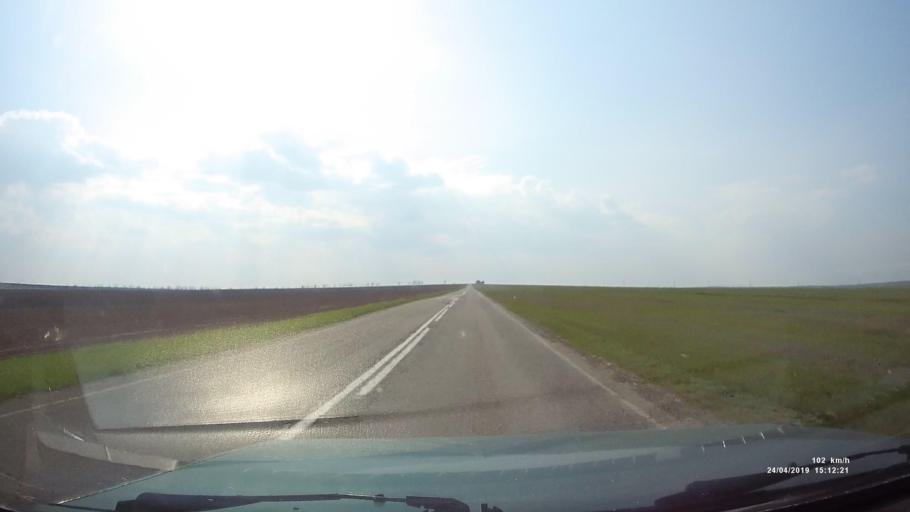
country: RU
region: Rostov
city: Remontnoye
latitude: 46.5464
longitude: 43.3024
